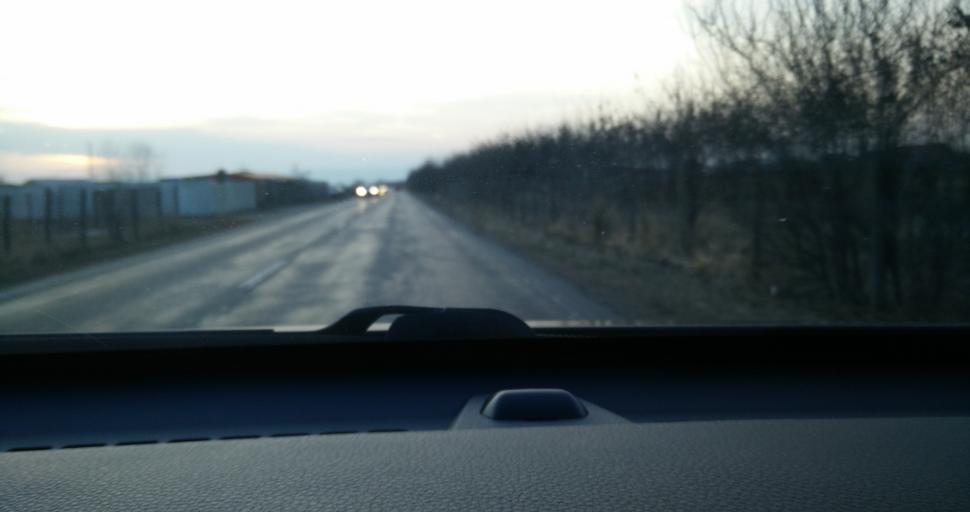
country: RO
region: Vrancea
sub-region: Comuna Milcovul
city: Milcovul
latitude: 45.6772
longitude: 27.2426
